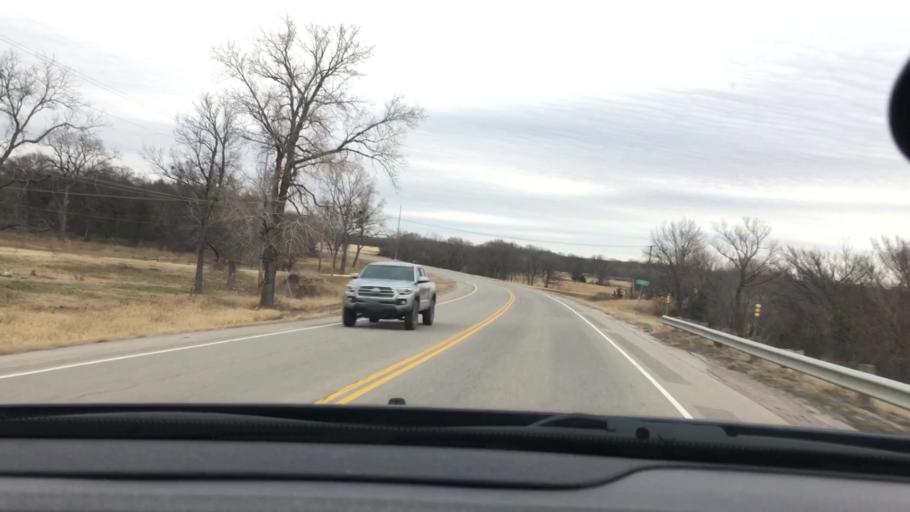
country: US
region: Oklahoma
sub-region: Marshall County
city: Oakland
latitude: 34.1887
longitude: -96.8044
